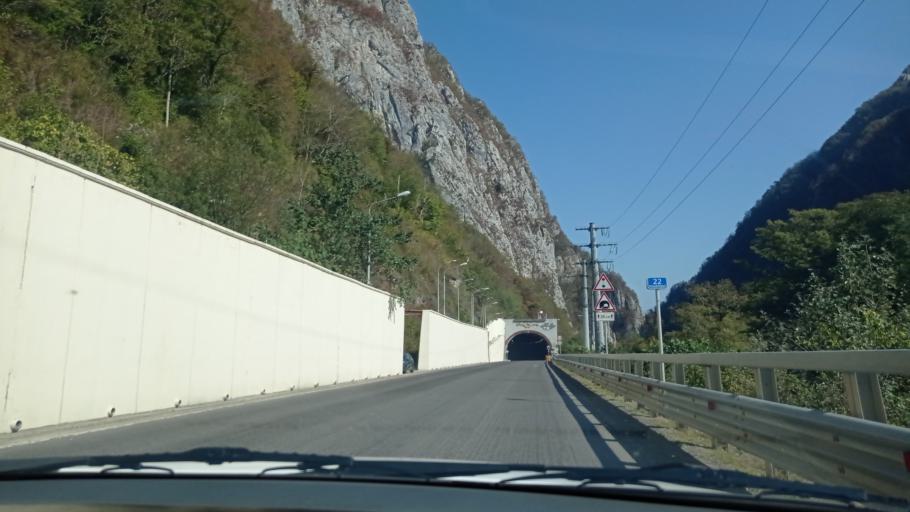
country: RU
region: Krasnodarskiy
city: Vysokoye
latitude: 43.5972
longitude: 40.0218
